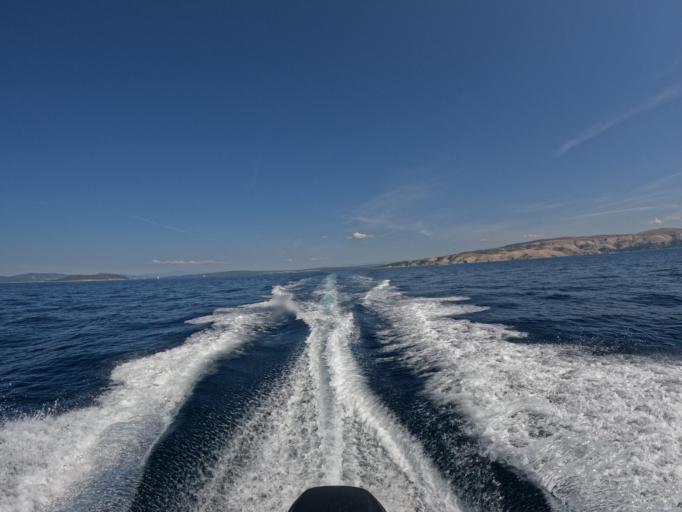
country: HR
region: Primorsko-Goranska
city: Punat
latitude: 44.9227
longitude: 14.6206
